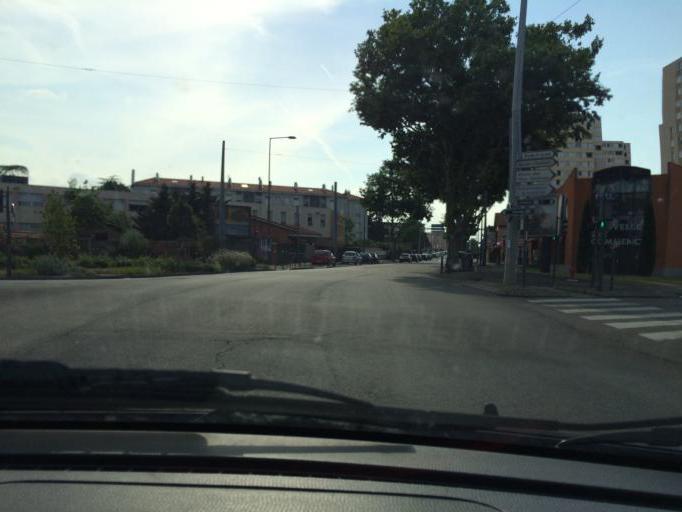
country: FR
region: Rhone-Alpes
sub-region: Departement du Rhone
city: Vaulx-en-Velin
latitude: 45.7634
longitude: 4.9137
